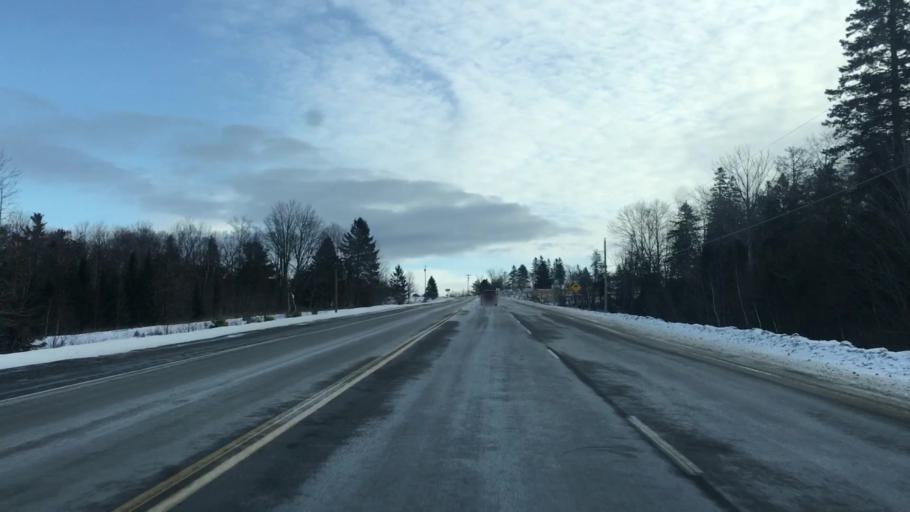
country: US
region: Maine
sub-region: Washington County
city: Machias
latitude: 44.9505
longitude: -67.6685
